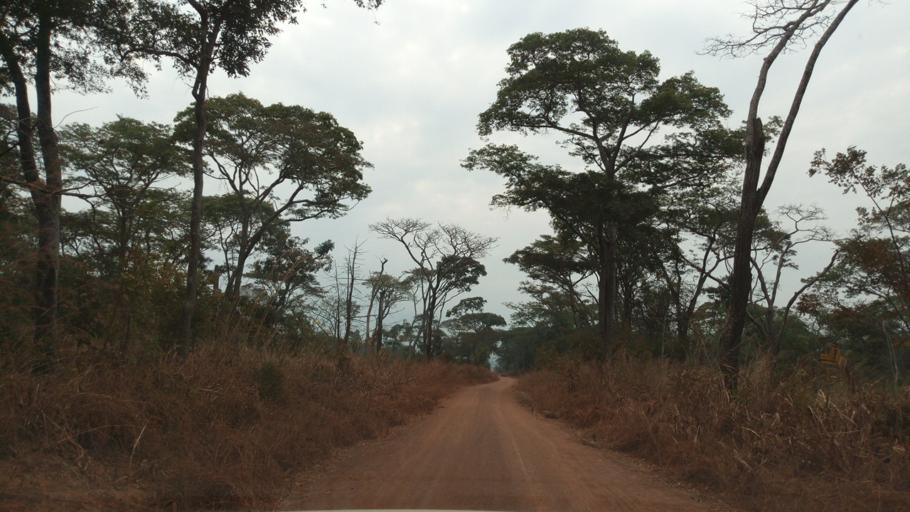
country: ZM
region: Northern
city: Kaputa
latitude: -8.1818
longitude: 29.0859
